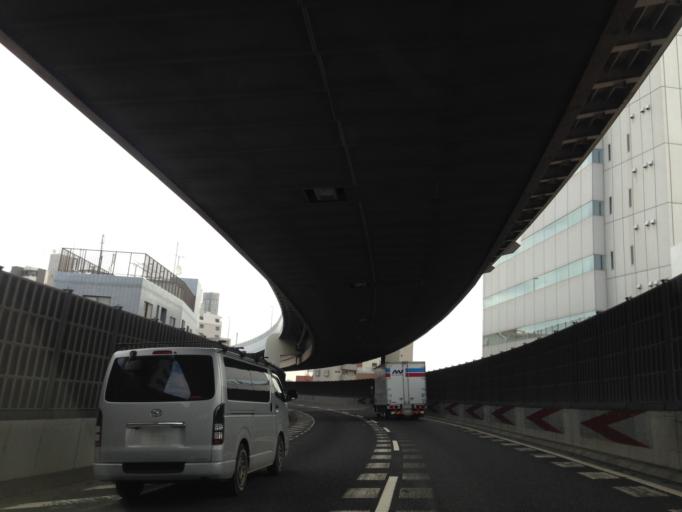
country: JP
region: Saitama
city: Kawaguchi
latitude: 35.7450
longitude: 139.7273
